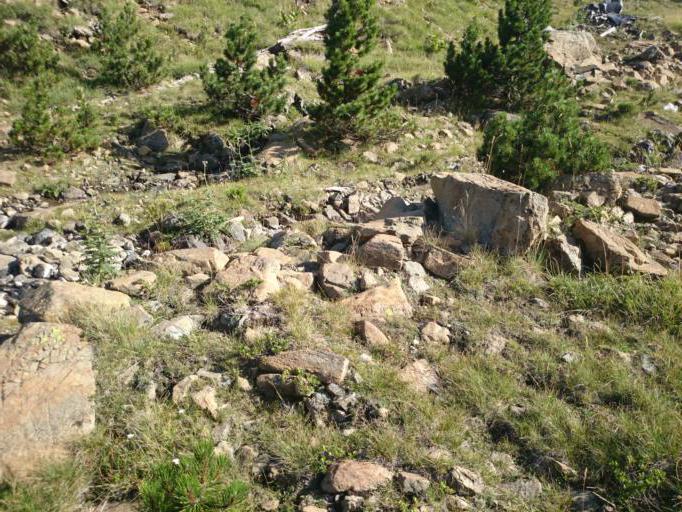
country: AL
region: Elbasan
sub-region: Rrethi i Gramshit
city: Lenias
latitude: 40.8223
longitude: 20.4627
